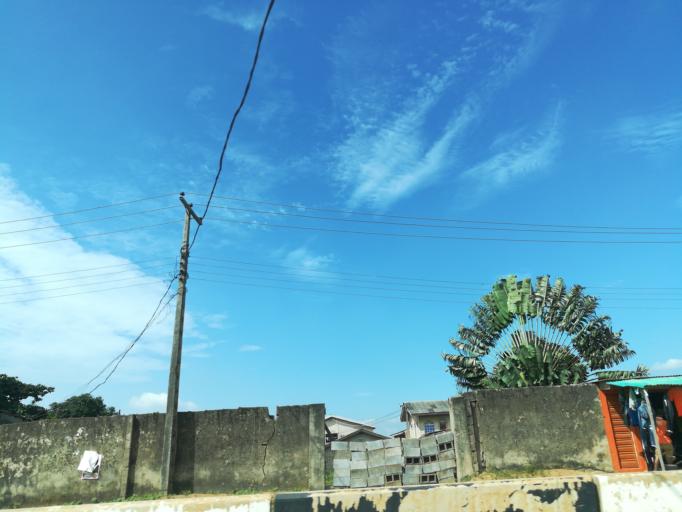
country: NG
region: Lagos
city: Ebute Ikorodu
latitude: 6.5933
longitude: 3.5066
